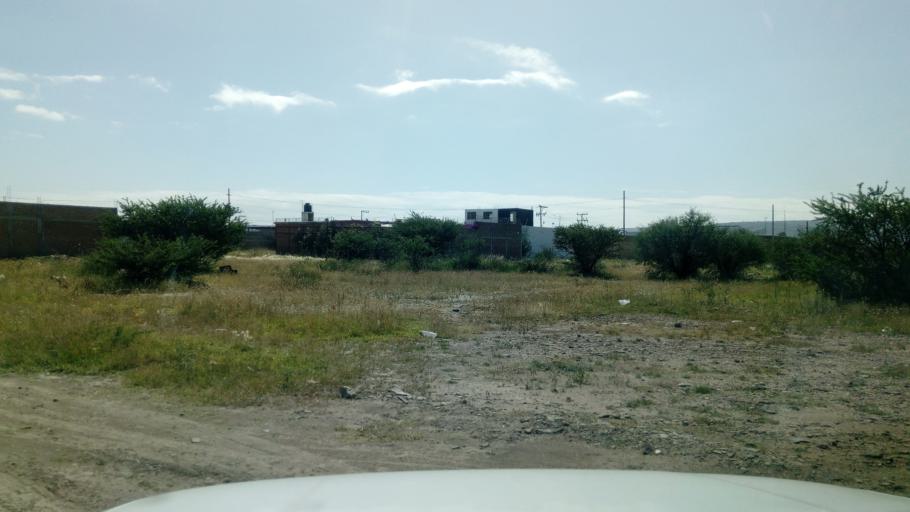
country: MX
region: Durango
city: Victoria de Durango
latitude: 23.9827
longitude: -104.6728
